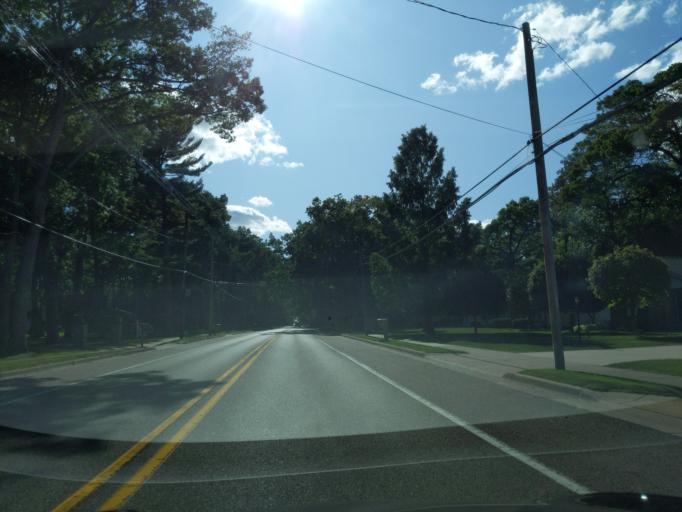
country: US
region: Michigan
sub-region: Muskegon County
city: North Muskegon
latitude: 43.2460
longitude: -86.2847
